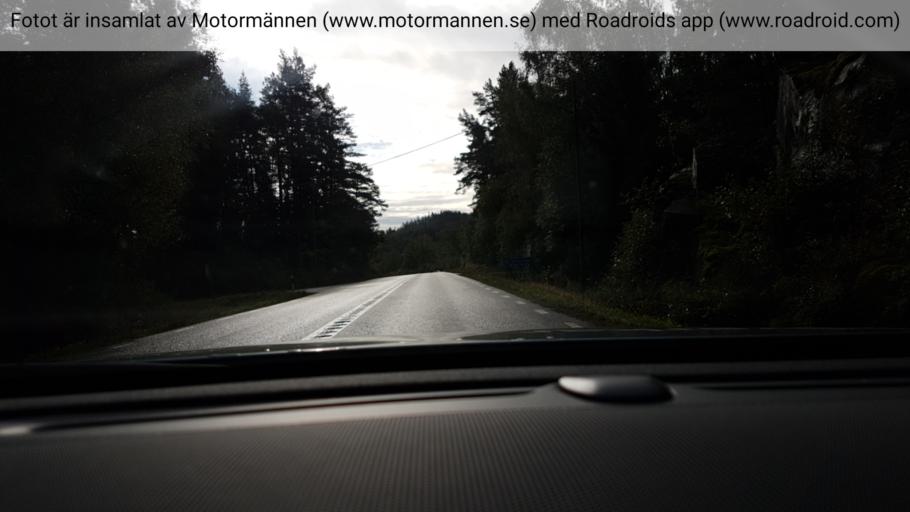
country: SE
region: Vaestra Goetaland
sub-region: Harryda Kommun
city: Ravlanda
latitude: 57.5812
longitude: 12.4925
